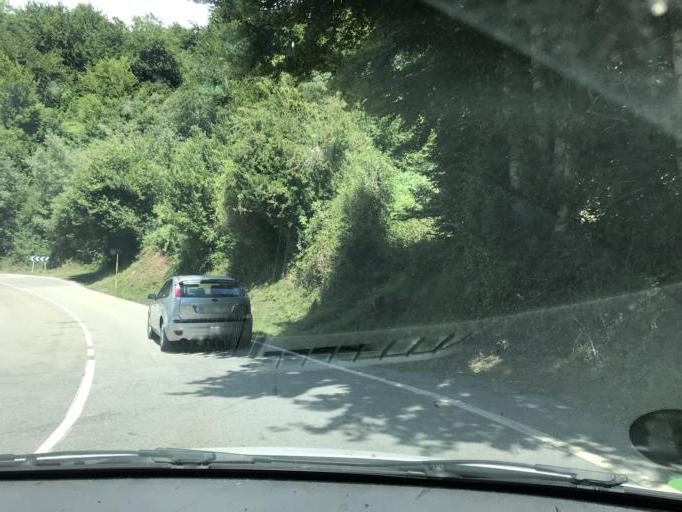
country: ES
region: Cantabria
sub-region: Provincia de Cantabria
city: Cabezon de Liebana
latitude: 43.0728
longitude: -4.4730
